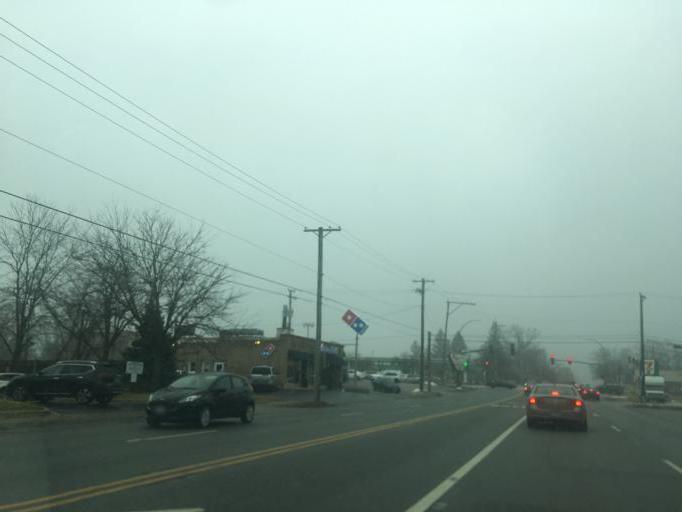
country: US
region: Illinois
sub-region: DuPage County
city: Downers Grove
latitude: 41.7858
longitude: -88.0375
